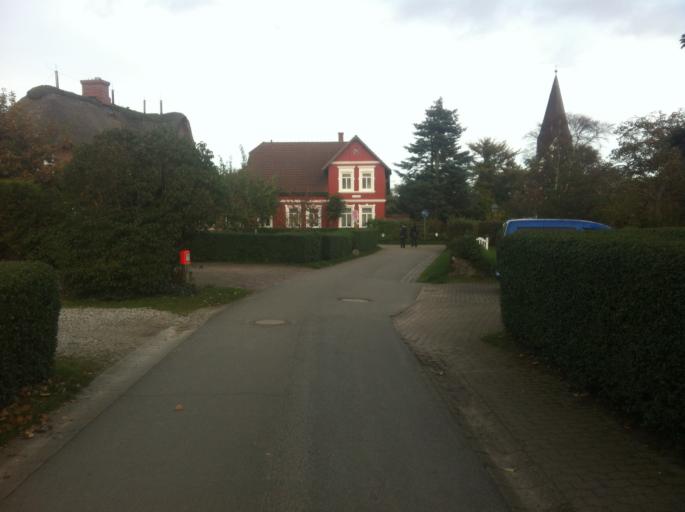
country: DE
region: Schleswig-Holstein
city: Nebel
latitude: 54.6529
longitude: 8.3539
